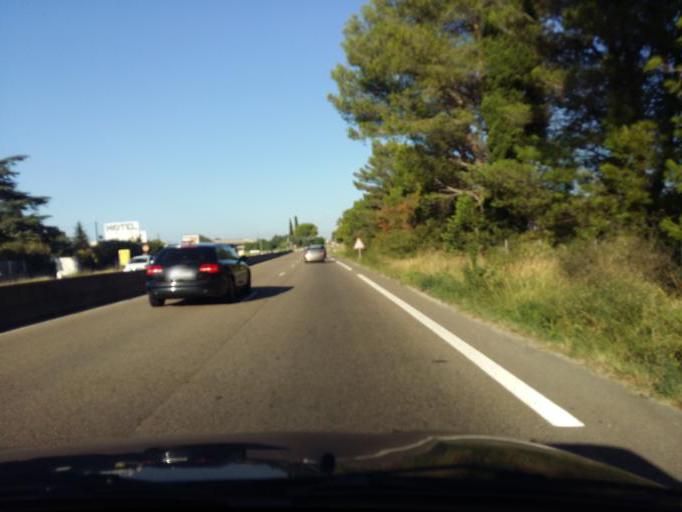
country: FR
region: Languedoc-Roussillon
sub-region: Departement du Gard
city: Marguerittes
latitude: 43.8588
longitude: 4.4251
